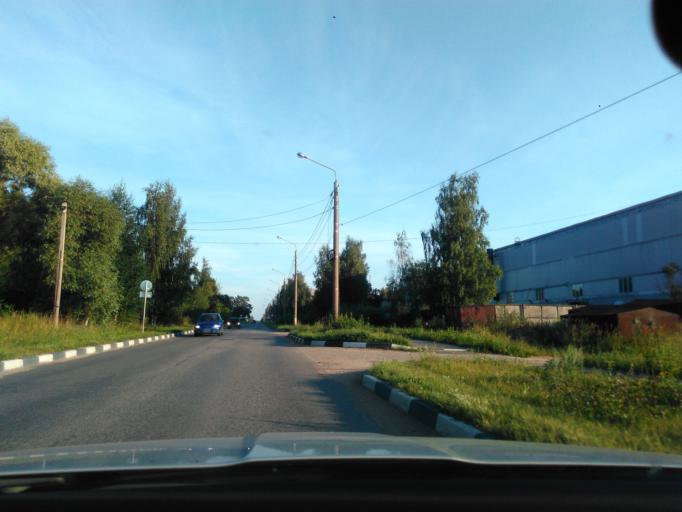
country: RU
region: Tverskaya
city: Konakovo
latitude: 56.7266
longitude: 36.7820
